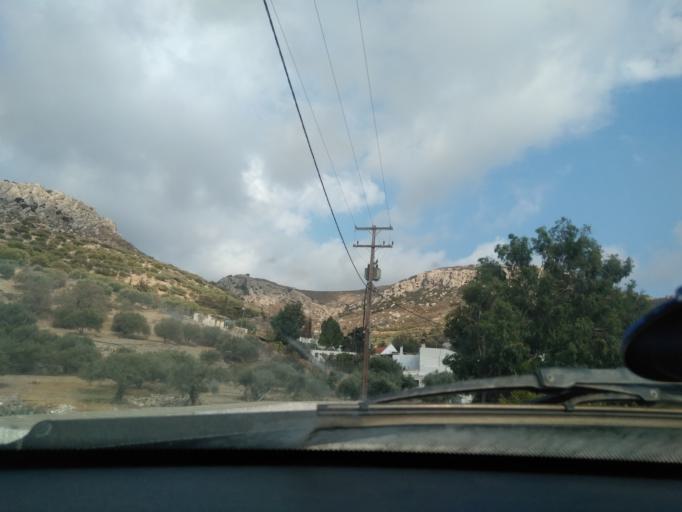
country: GR
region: Crete
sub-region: Nomos Lasithiou
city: Makry-Gialos
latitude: 35.0459
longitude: 26.0585
